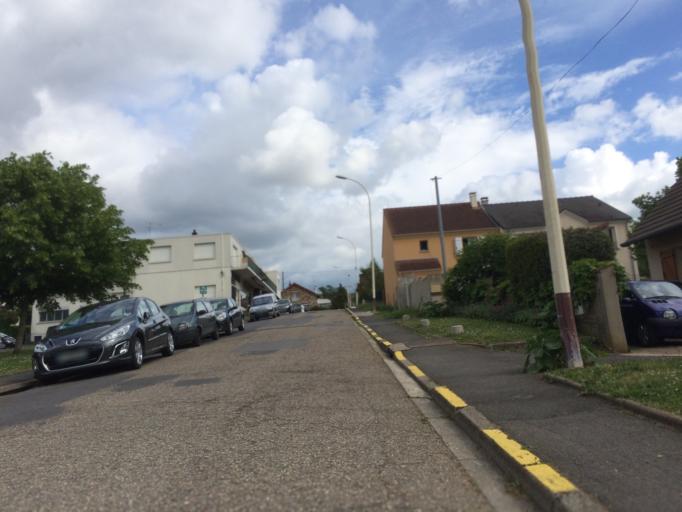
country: FR
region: Ile-de-France
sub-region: Departement de l'Essonne
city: Villiers-sur-Orge
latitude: 48.6512
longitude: 2.3056
